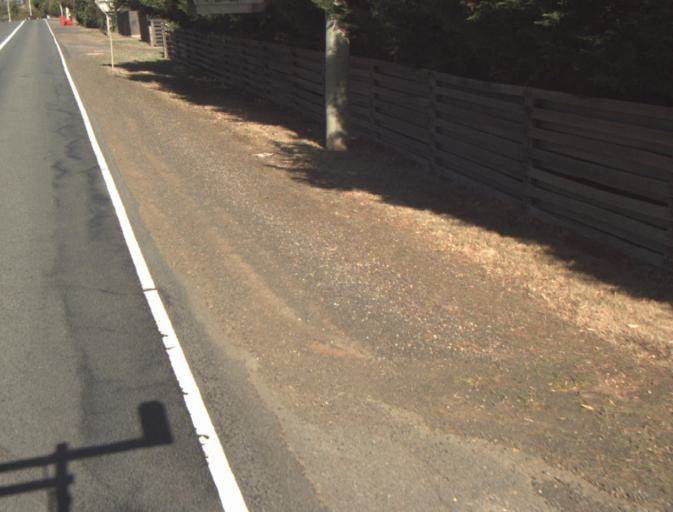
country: AU
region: Tasmania
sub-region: Launceston
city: Mayfield
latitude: -41.3381
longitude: 147.0828
